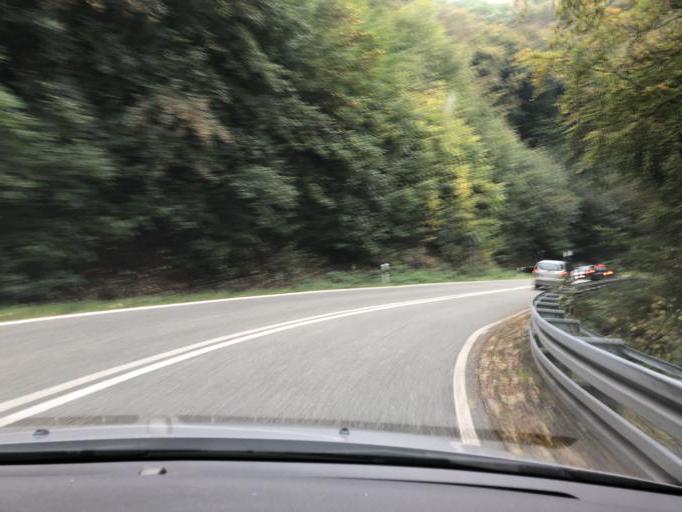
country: DE
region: Saxony-Anhalt
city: Kelbra
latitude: 51.4160
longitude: 11.0682
